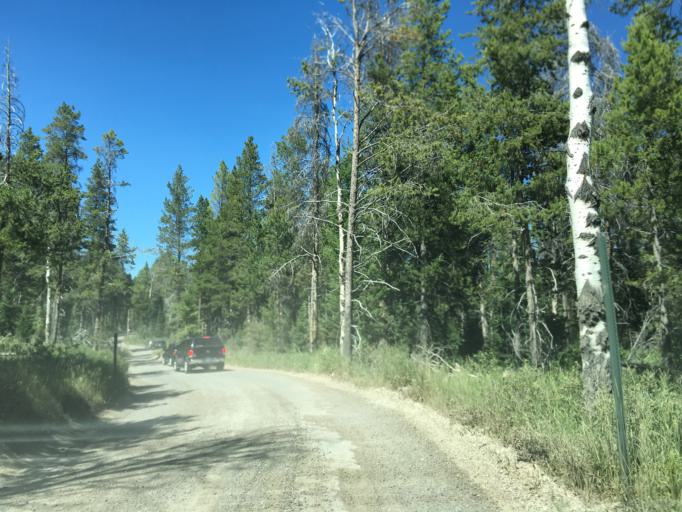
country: US
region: Wyoming
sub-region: Teton County
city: Moose Wilson Road
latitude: 43.6145
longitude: -110.7915
